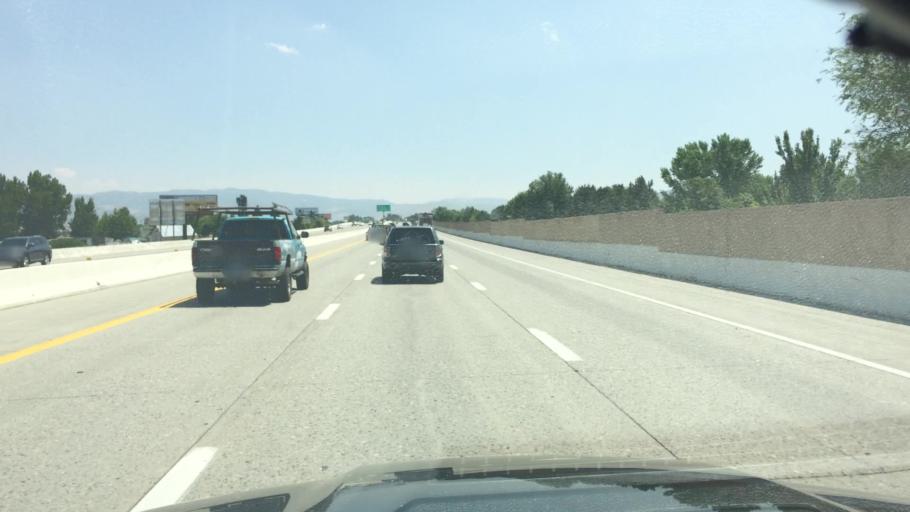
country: US
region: Nevada
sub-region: Washoe County
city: Reno
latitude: 39.4603
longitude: -119.7846
